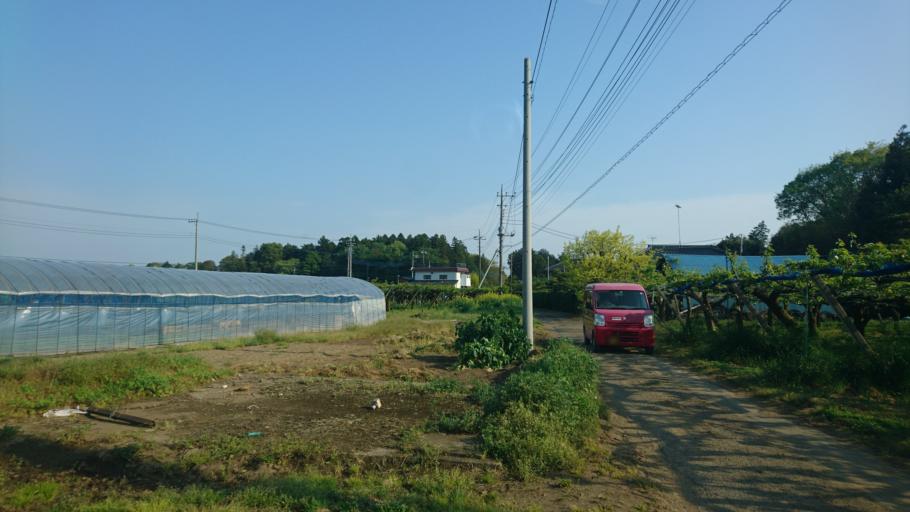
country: JP
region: Ibaraki
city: Shimodate
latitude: 36.2380
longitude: 139.9502
